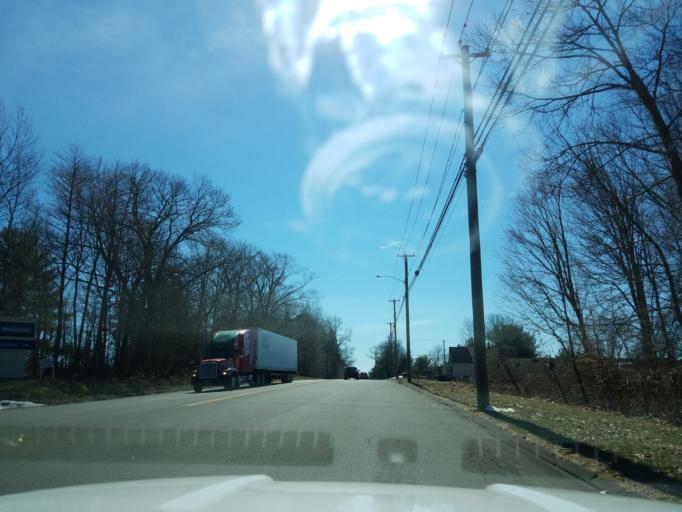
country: US
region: Connecticut
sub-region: New Haven County
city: Woodmont
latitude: 41.2498
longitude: -72.9995
